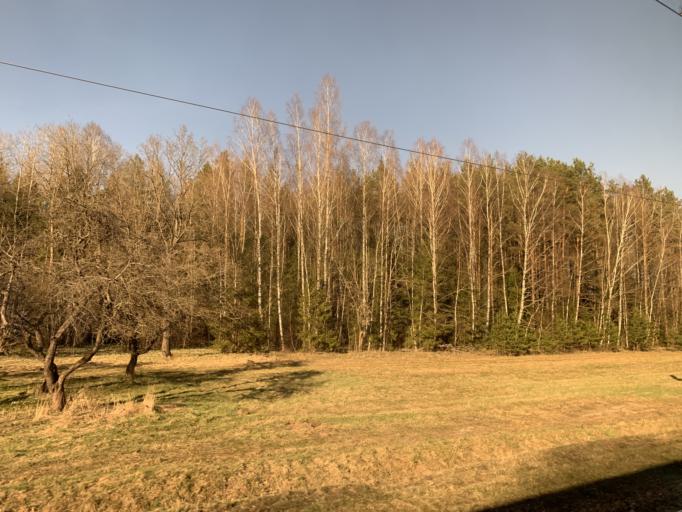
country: BY
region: Grodnenskaya
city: Smarhon'
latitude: 54.4853
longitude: 26.3202
